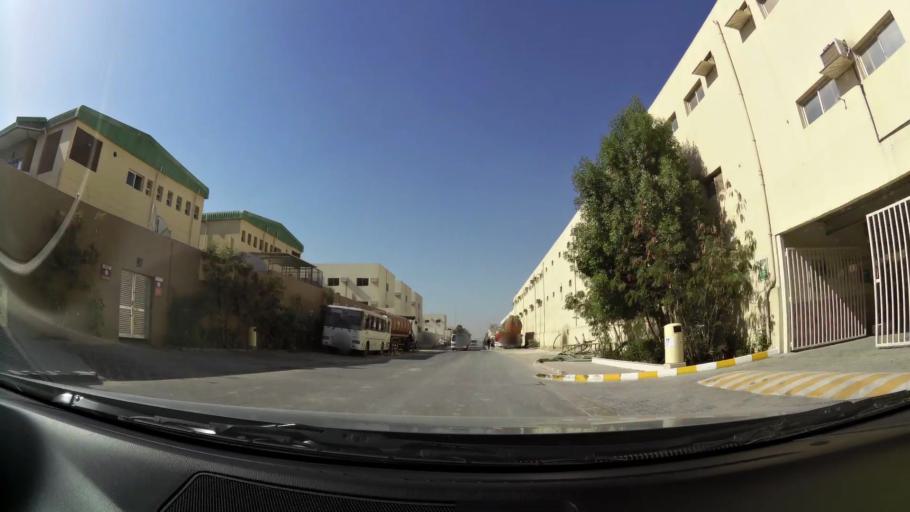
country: AE
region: Dubai
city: Dubai
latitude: 25.0074
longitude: 55.1026
